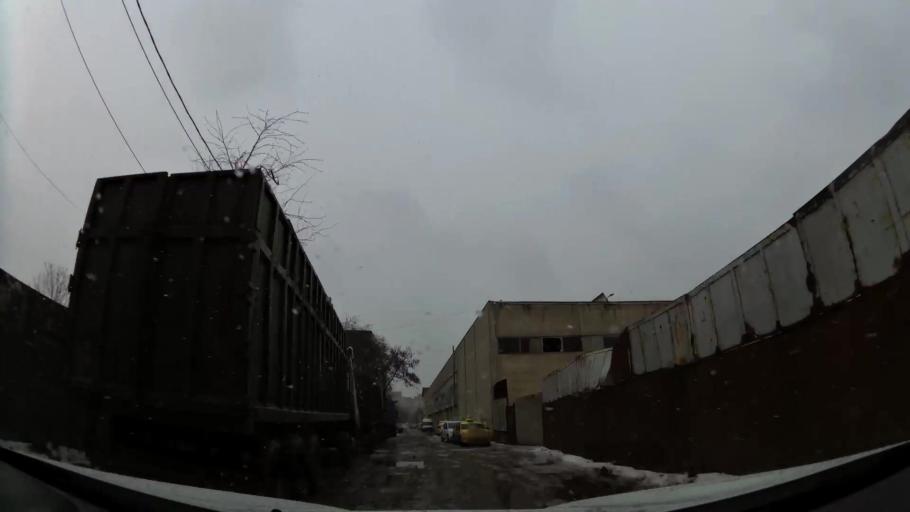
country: RO
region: Ilfov
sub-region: Comuna Chiajna
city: Rosu
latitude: 44.4293
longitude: 26.0073
